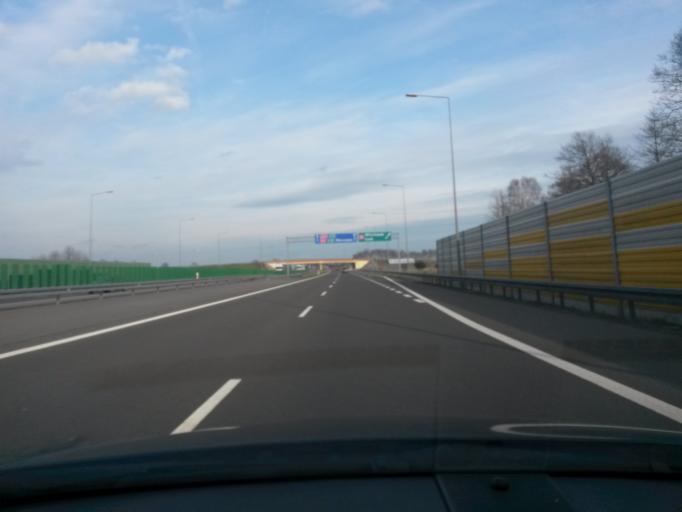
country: PL
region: Lodz Voivodeship
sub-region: Powiat zgierski
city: Ozorkow
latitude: 51.9225
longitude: 19.3476
